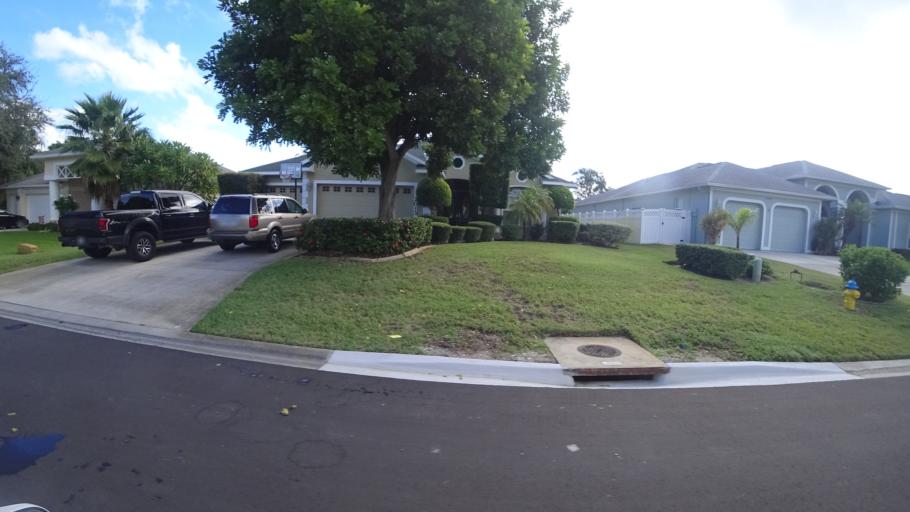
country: US
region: Florida
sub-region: Manatee County
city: West Bradenton
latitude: 27.5175
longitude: -82.6533
